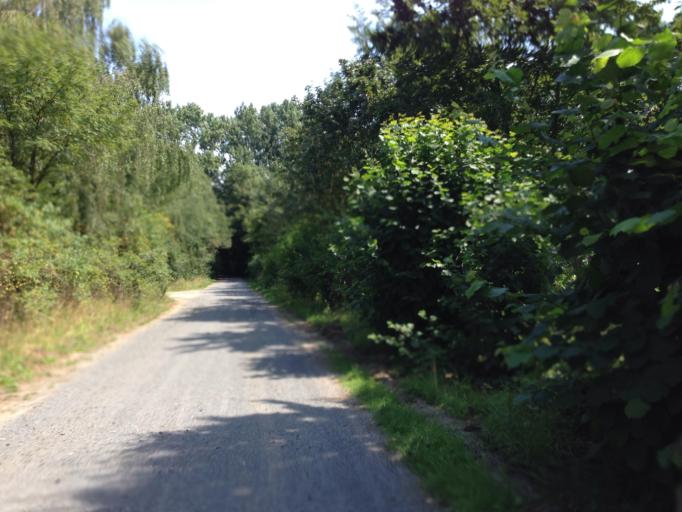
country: DE
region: Hesse
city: Dreieich
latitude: 50.0133
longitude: 8.7347
